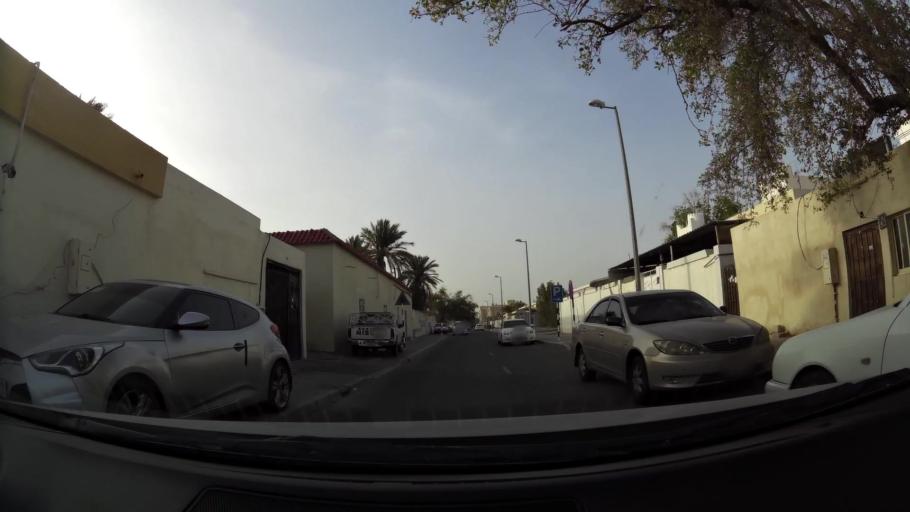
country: OM
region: Al Buraimi
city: Al Buraymi
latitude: 24.2430
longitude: 55.7499
